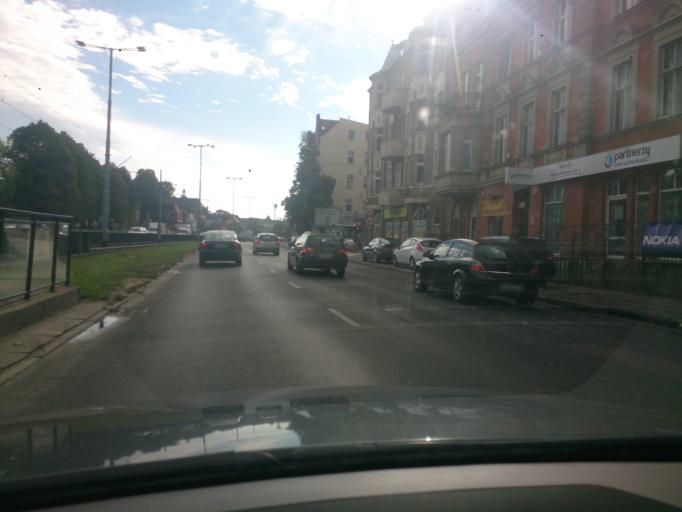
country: PL
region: Pomeranian Voivodeship
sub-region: Gdansk
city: Gdansk
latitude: 54.3757
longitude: 18.6155
